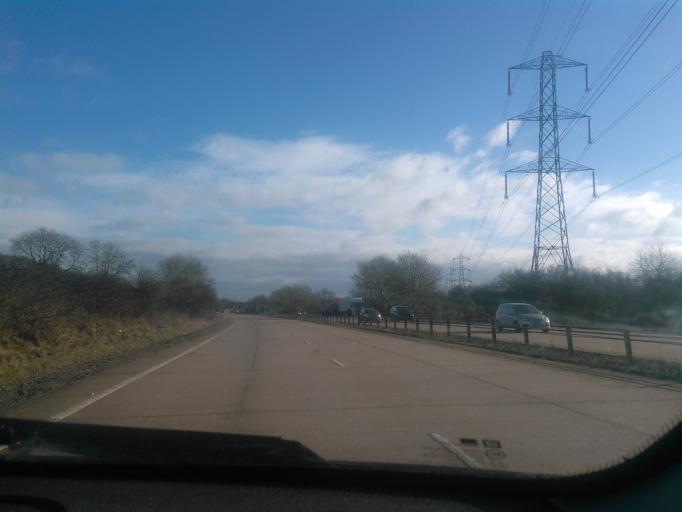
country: GB
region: England
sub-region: Staffordshire
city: Uttoxeter
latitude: 52.9227
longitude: -1.9330
